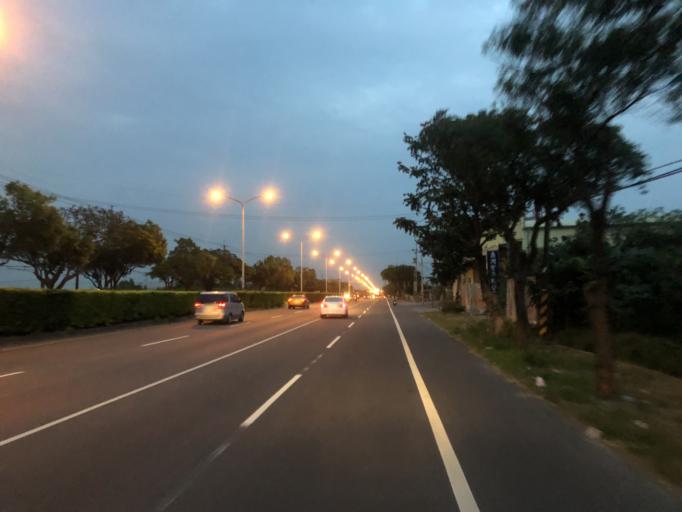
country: TW
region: Taiwan
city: Yujing
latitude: 23.1450
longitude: 120.3281
